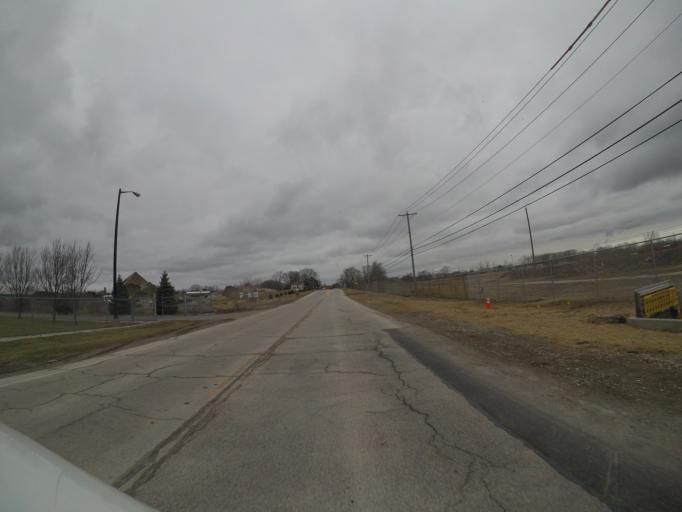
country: US
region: Ohio
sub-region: Wood County
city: Walbridge
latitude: 41.6138
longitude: -83.5125
